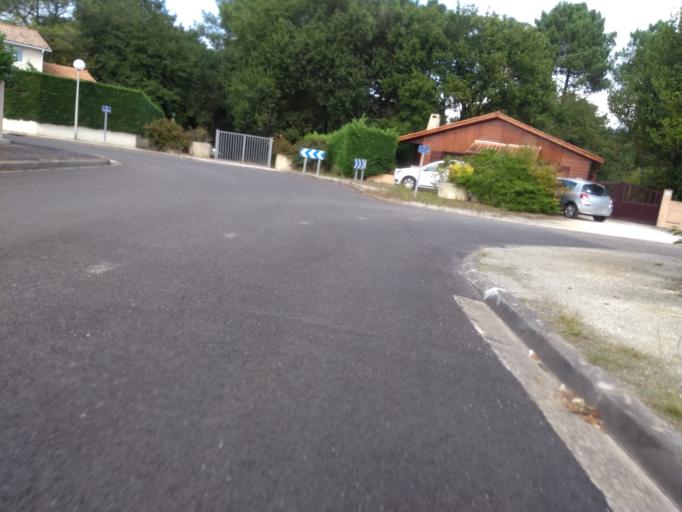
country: FR
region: Aquitaine
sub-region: Departement de la Gironde
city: Gradignan
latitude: 44.7838
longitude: -0.6236
